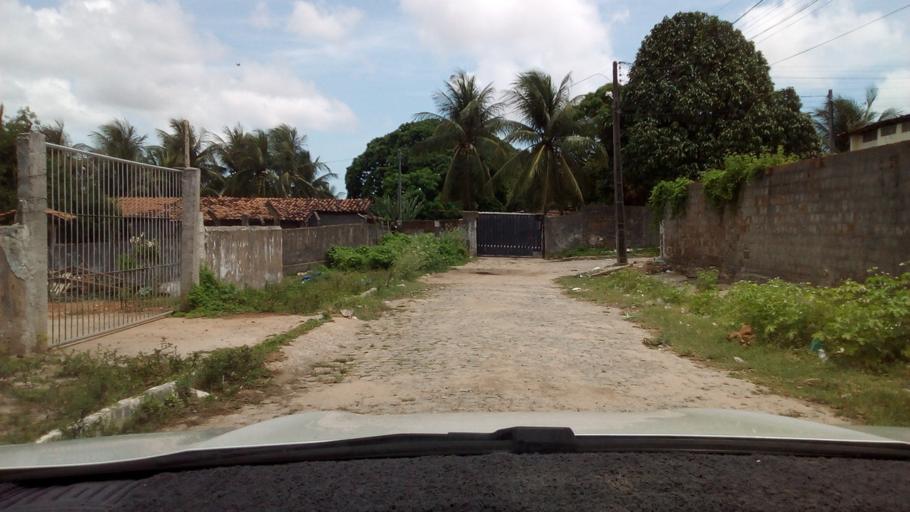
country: BR
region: Paraiba
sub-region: Joao Pessoa
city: Joao Pessoa
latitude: -7.1817
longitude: -34.8490
